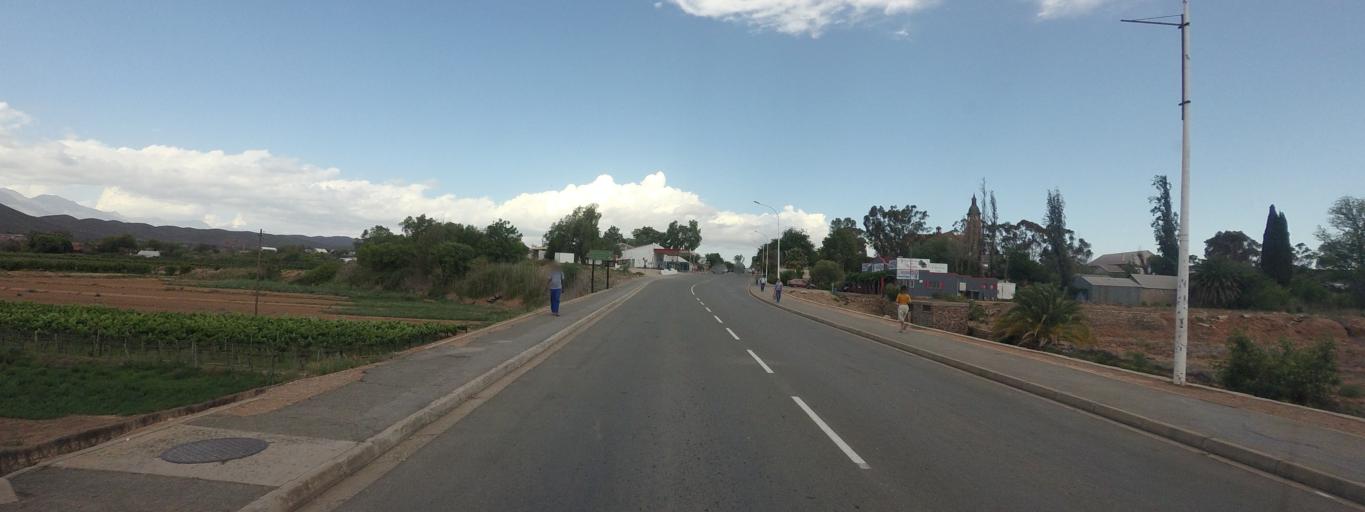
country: ZA
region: Western Cape
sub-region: Eden District Municipality
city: Ladismith
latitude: -33.5300
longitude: 21.6861
